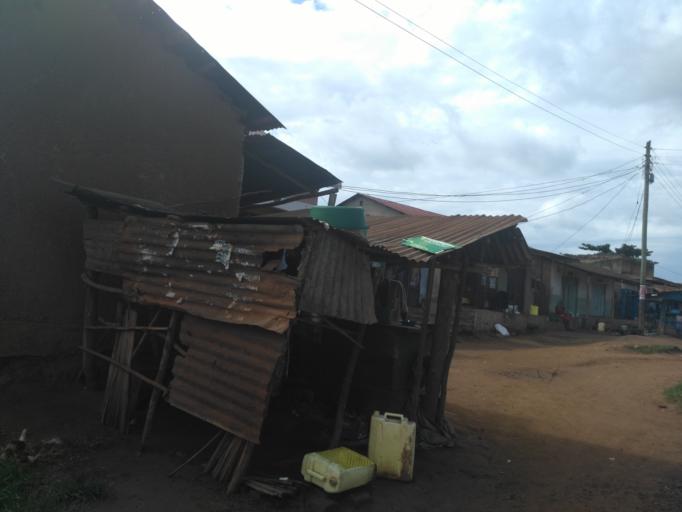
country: UG
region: Central Region
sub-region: Buikwe District
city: Njeru
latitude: 0.3905
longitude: 33.1686
